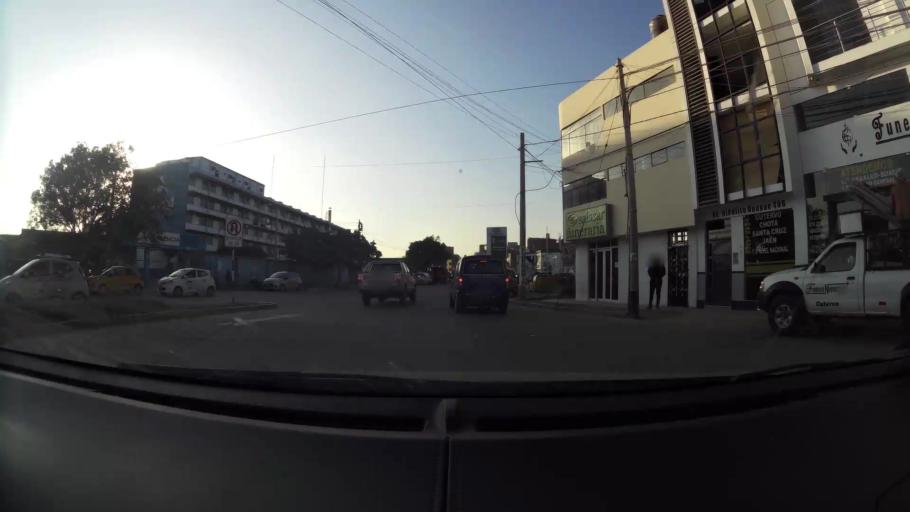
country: PE
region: Lambayeque
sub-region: Provincia de Chiclayo
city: Santa Rosa
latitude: -6.7740
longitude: -79.8293
